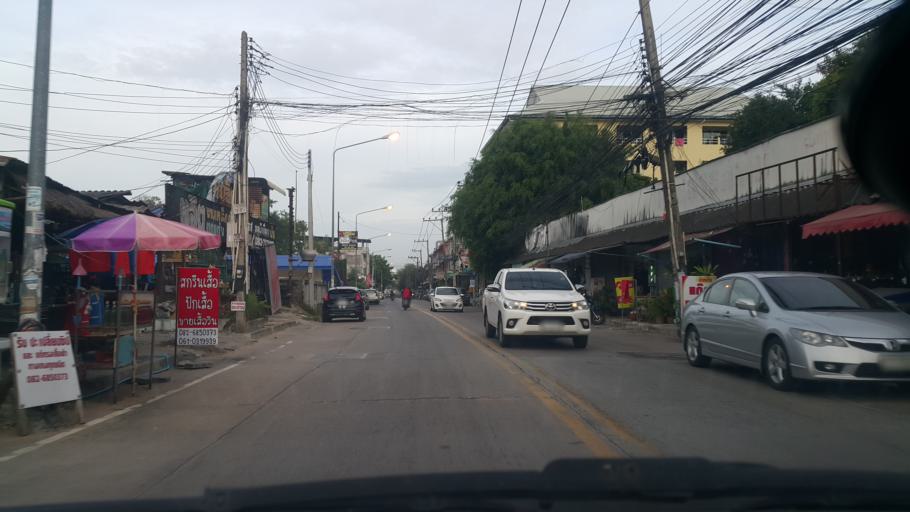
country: TH
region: Chon Buri
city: Phatthaya
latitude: 12.9535
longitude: 100.9031
